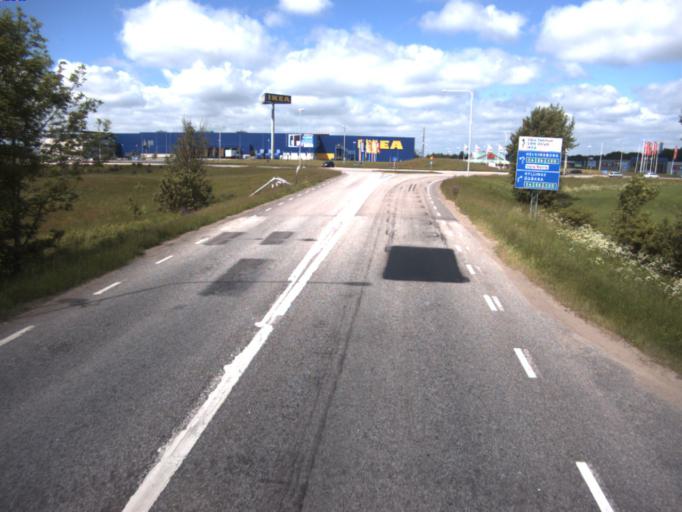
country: SE
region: Skane
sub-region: Helsingborg
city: Odakra
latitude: 56.0896
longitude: 12.7648
